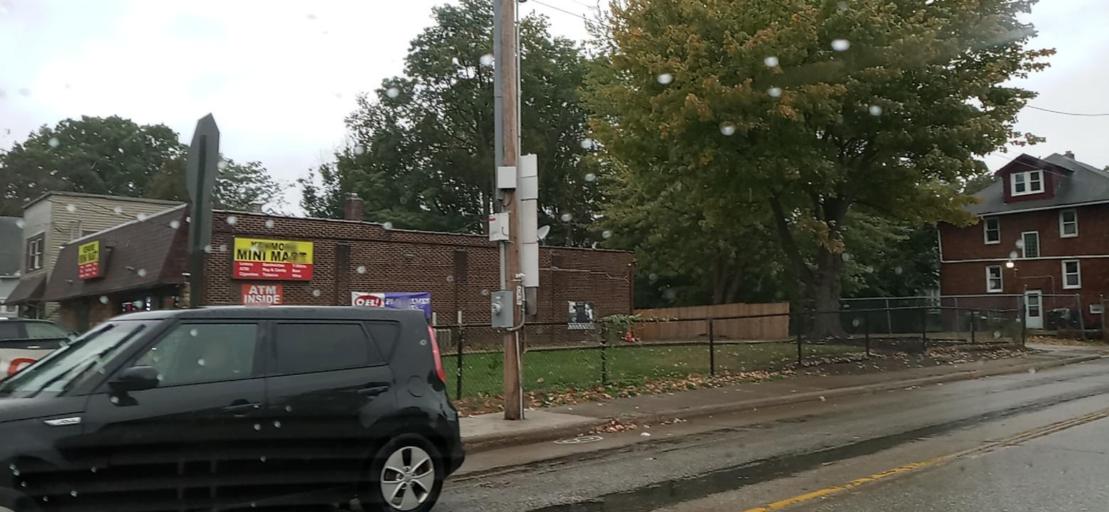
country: US
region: Ohio
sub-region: Summit County
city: Barberton
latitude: 41.0416
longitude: -81.5666
